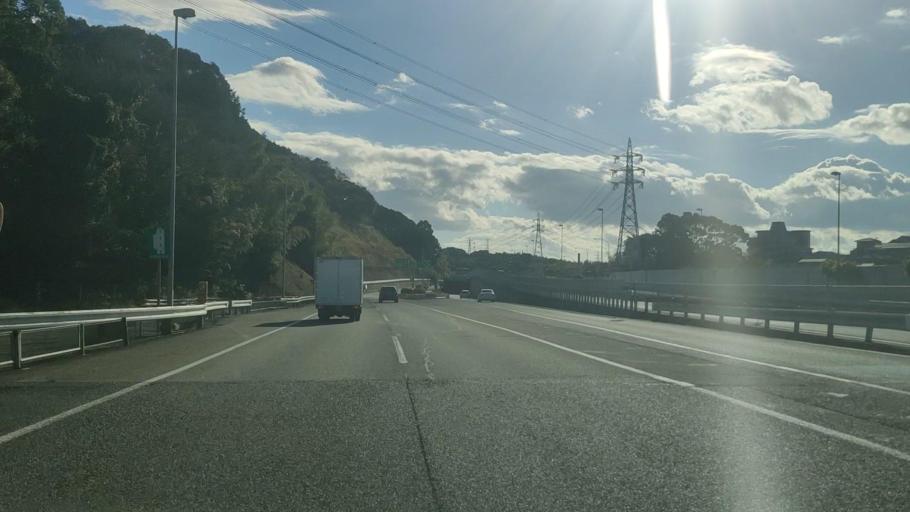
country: JP
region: Fukuoka
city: Kitakyushu
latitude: 33.8470
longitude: 130.7667
